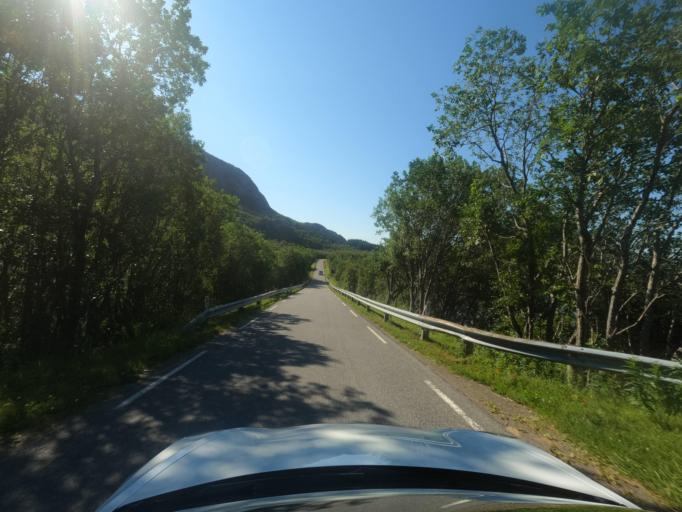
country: NO
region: Nordland
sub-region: Hadsel
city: Stokmarknes
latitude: 68.3238
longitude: 15.0063
